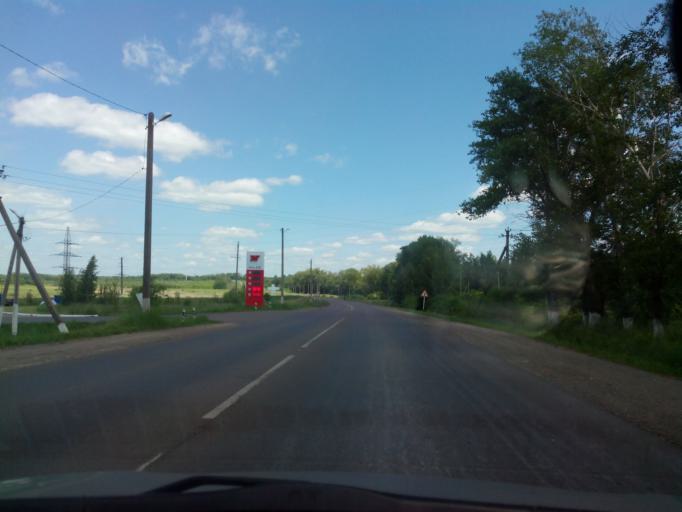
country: RU
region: Tambov
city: Zherdevka
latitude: 51.8341
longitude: 41.5018
